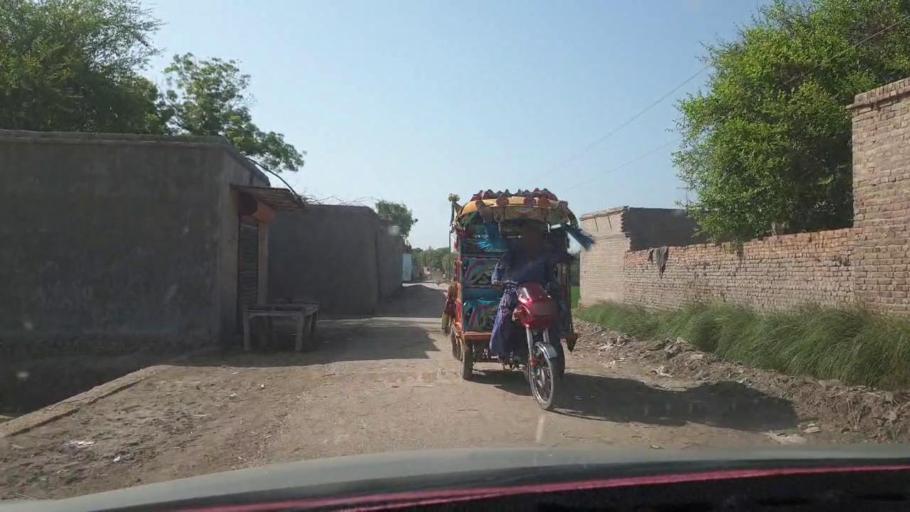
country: PK
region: Sindh
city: Nasirabad
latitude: 27.3832
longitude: 67.8786
